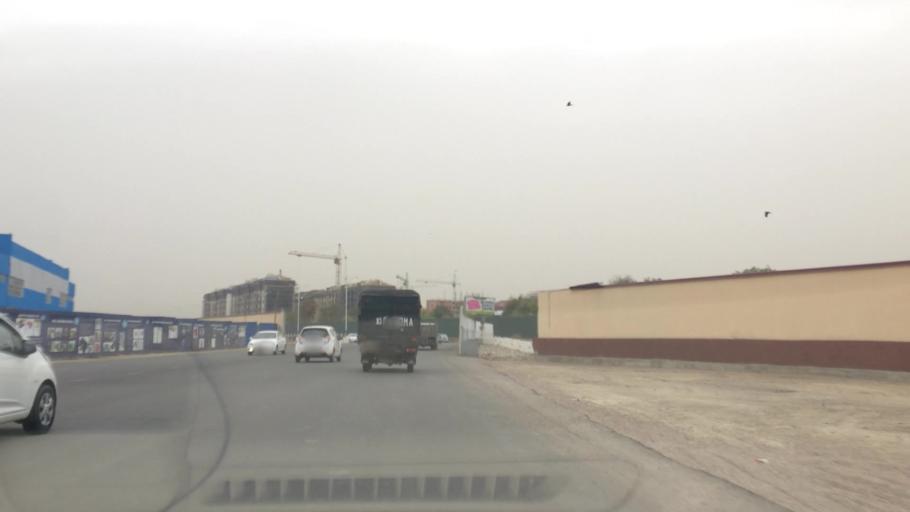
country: UZ
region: Toshkent
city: Salor
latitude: 41.3052
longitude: 69.3361
